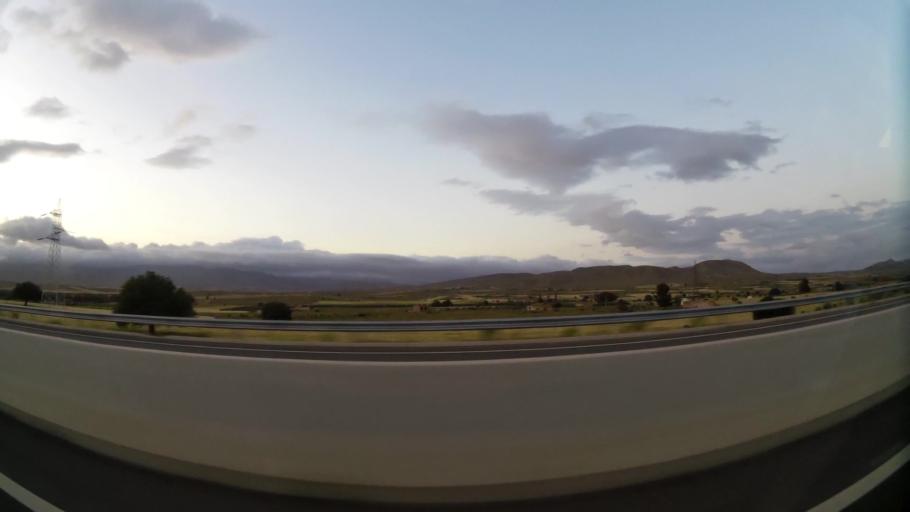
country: MA
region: Oriental
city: El Aioun
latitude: 34.6237
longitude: -2.5015
